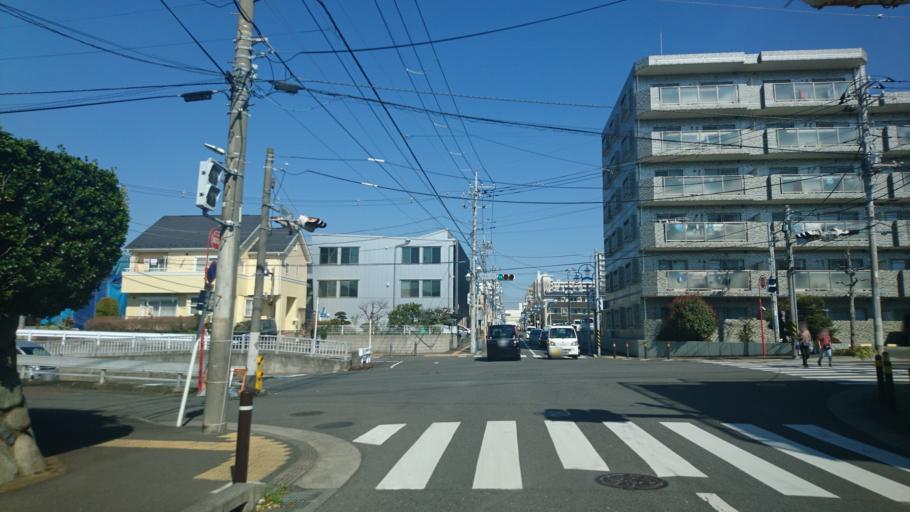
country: JP
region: Kanagawa
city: Fujisawa
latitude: 35.3930
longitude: 139.4692
